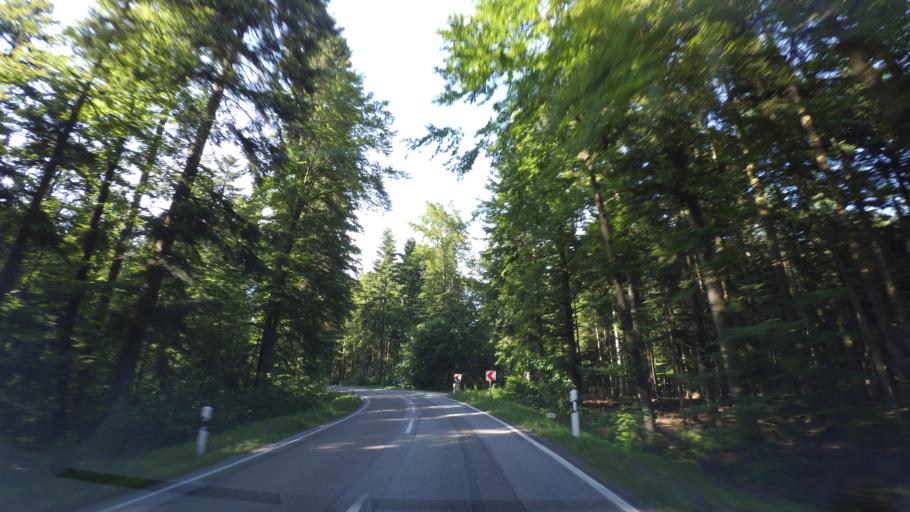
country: DE
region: Baden-Wuerttemberg
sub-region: Regierungsbezirk Stuttgart
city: Gschwend
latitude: 48.9267
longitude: 9.7073
